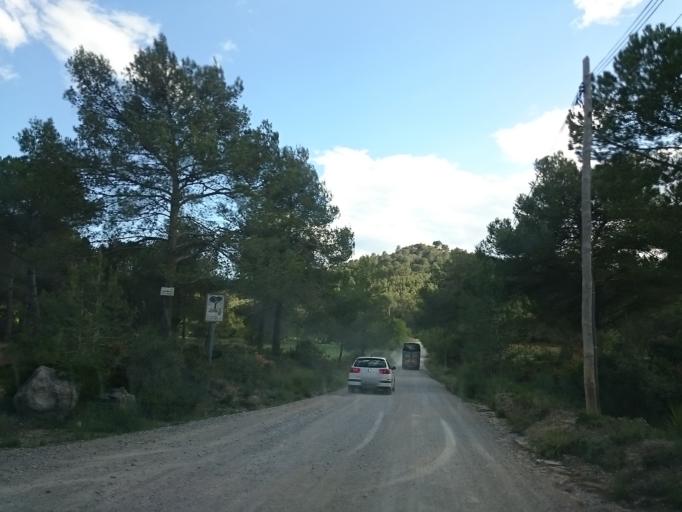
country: ES
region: Catalonia
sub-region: Provincia de Barcelona
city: Begues
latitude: 41.3256
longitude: 1.9255
